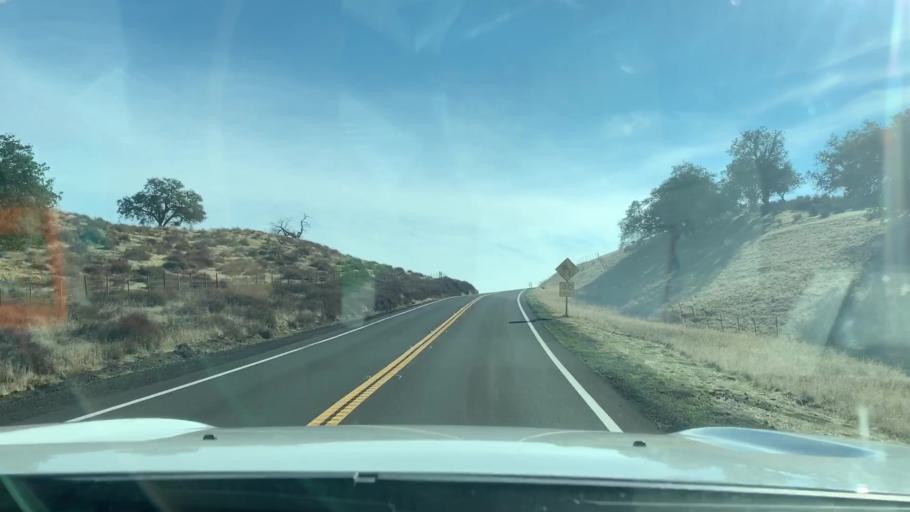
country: US
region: California
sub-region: Fresno County
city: Coalinga
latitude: 36.0930
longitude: -120.5155
